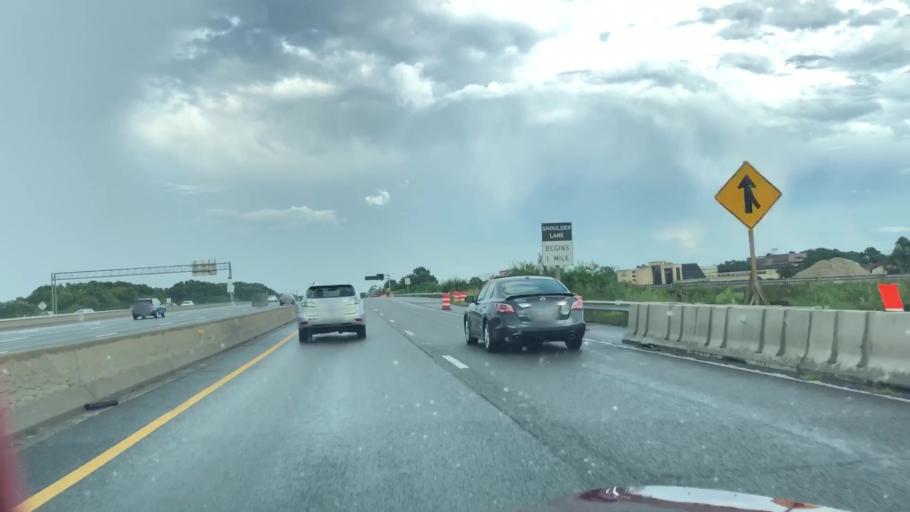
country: US
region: Virginia
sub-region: City of Chesapeake
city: Chesapeake
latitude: 36.8449
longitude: -76.1869
